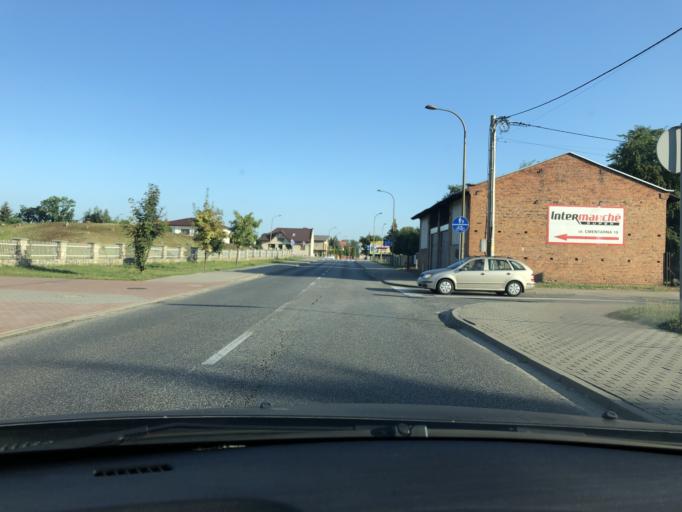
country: PL
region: Lodz Voivodeship
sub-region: Powiat wieruszowski
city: Wieruszow
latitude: 51.2903
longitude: 18.1617
